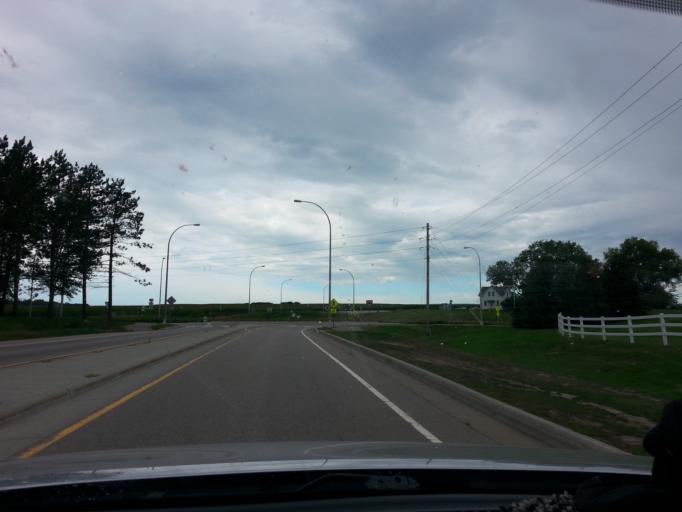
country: US
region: Minnesota
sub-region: Scott County
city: Prior Lake
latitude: 44.6673
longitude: -93.3395
